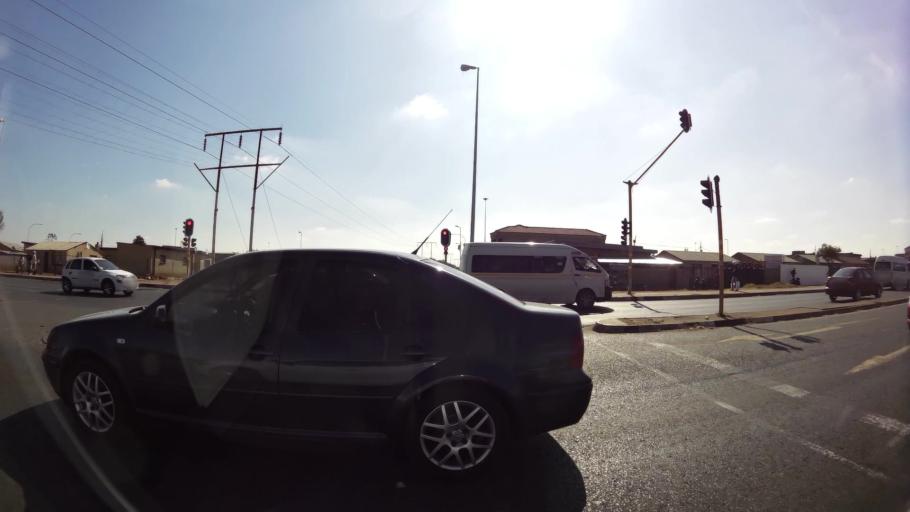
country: ZA
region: Gauteng
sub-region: City of Johannesburg Metropolitan Municipality
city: Soweto
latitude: -26.2794
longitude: 27.8627
